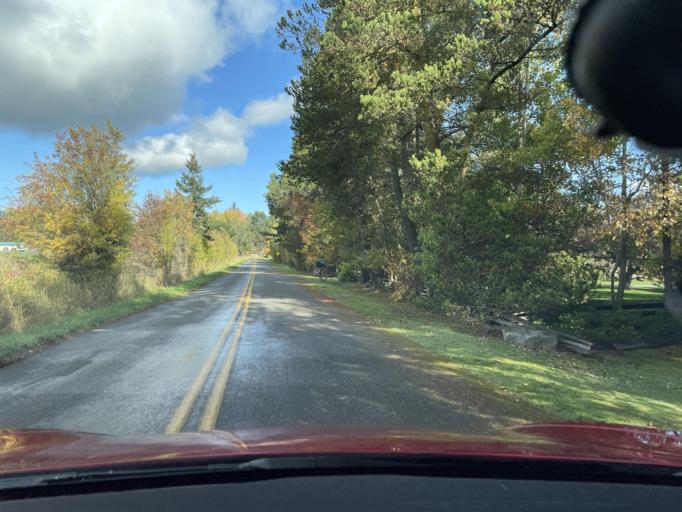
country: US
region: Washington
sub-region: San Juan County
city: Friday Harbor
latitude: 48.5015
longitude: -123.0230
